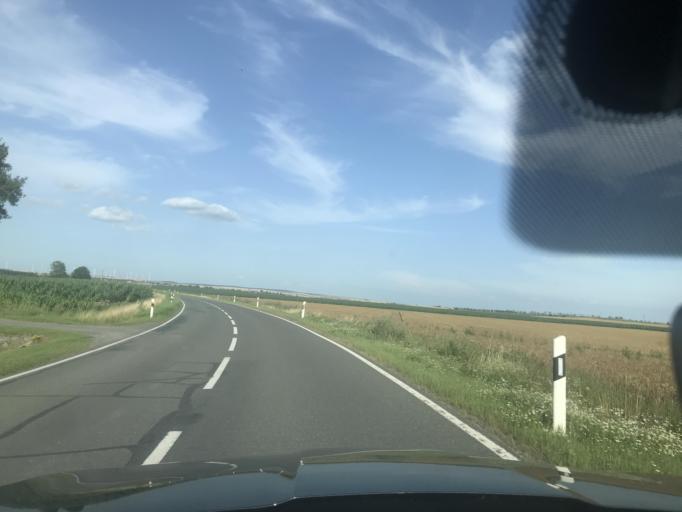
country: DE
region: Saxony-Anhalt
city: Harsleben
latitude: 51.8698
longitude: 11.1217
